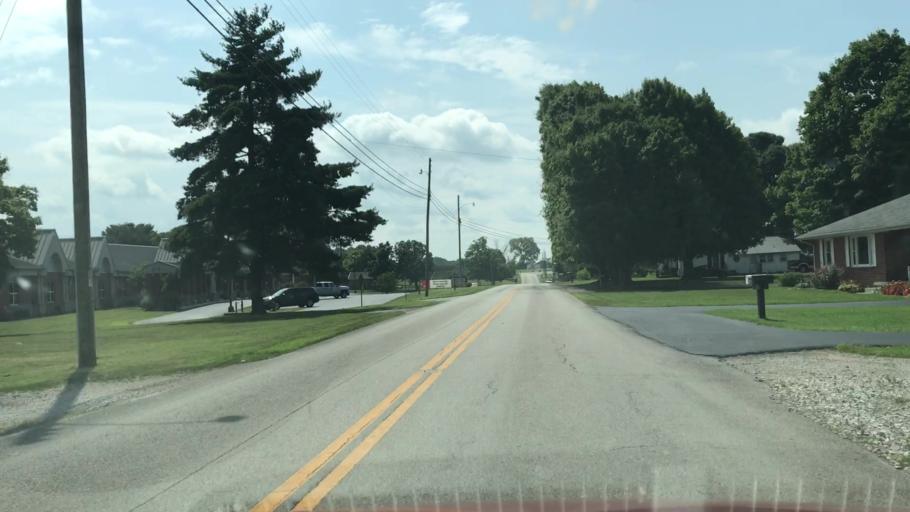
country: US
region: Kentucky
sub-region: Barren County
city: Glasgow
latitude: 36.8871
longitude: -85.8480
